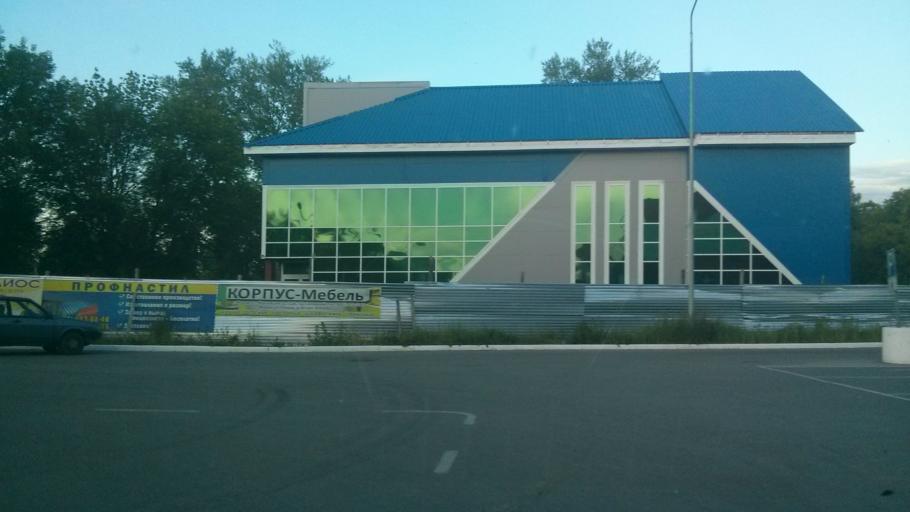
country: RU
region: Vladimir
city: Murom
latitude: 55.5472
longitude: 42.0667
